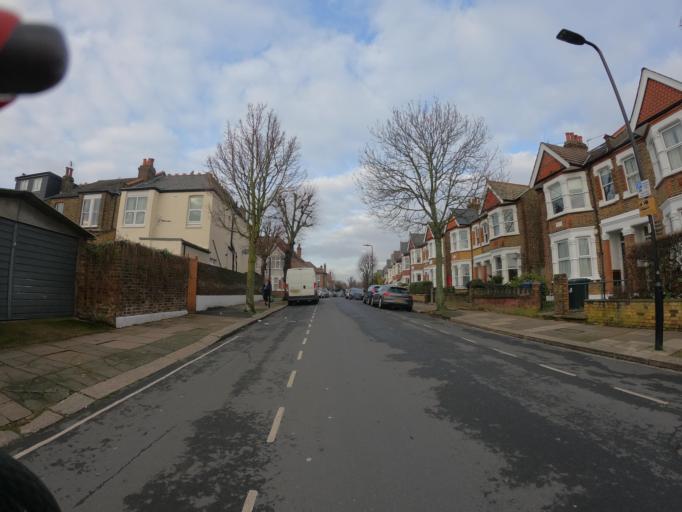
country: GB
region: England
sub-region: Greater London
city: Greenford
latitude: 51.5152
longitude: -0.3311
